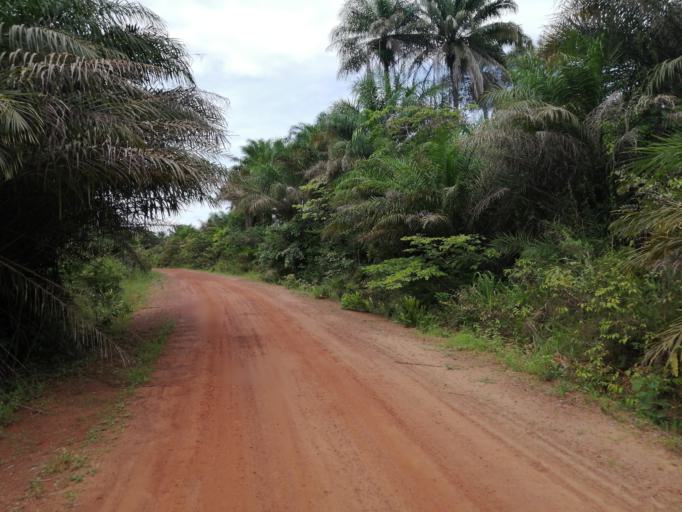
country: SL
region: Northern Province
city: Port Loko
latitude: 8.7784
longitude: -12.9200
